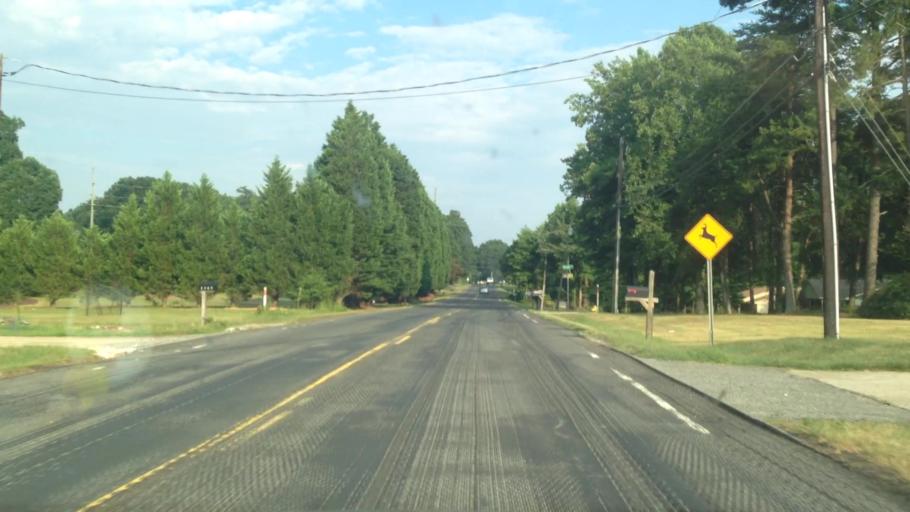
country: US
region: North Carolina
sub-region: Forsyth County
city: Kernersville
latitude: 36.0487
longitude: -80.0636
